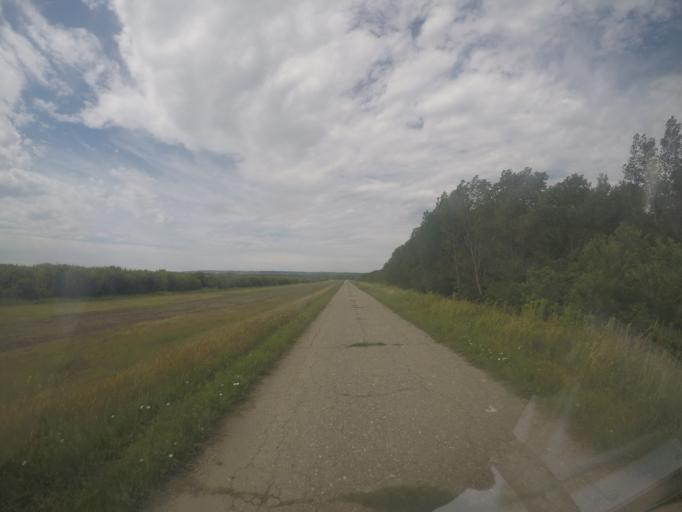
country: RS
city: Knicanin
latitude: 45.1773
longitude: 20.2984
